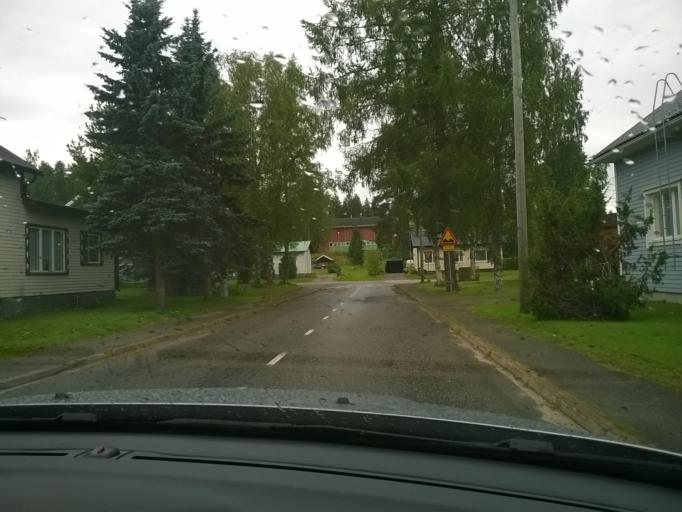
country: FI
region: Kainuu
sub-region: Kehys-Kainuu
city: Kuhmo
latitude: 64.1238
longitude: 29.5167
